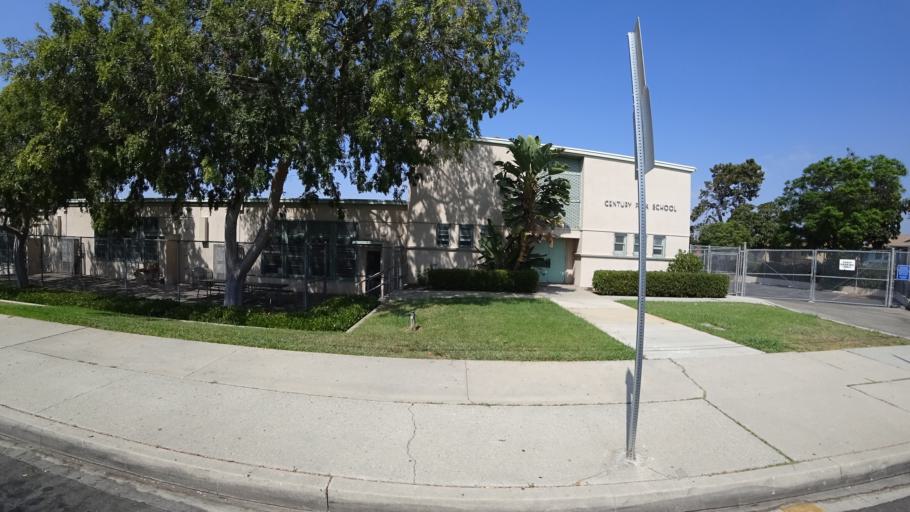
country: US
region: California
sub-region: Los Angeles County
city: Westmont
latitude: 33.9372
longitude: -118.3189
